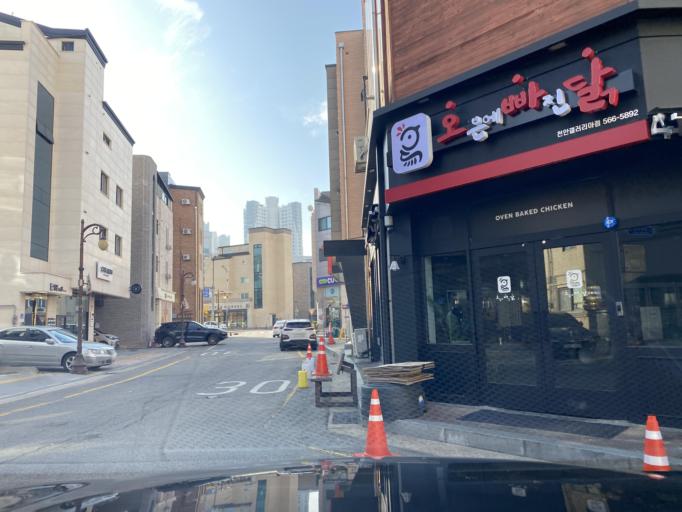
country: KR
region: Chungcheongnam-do
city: Cheonan
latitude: 36.8009
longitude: 127.1075
